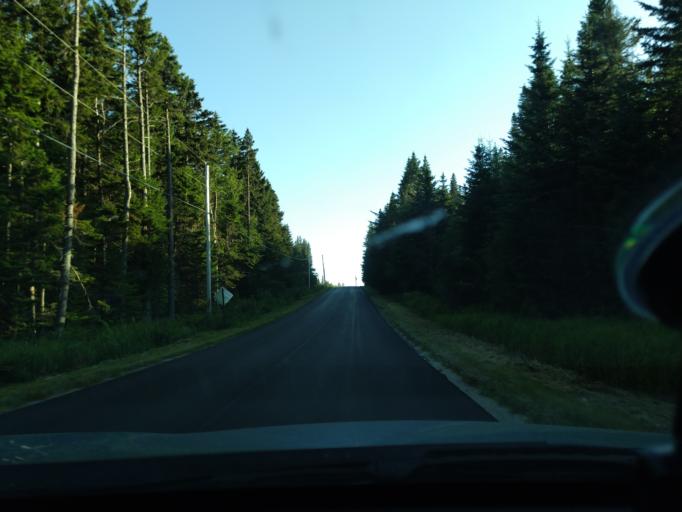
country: US
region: Maine
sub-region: Washington County
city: Machiasport
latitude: 44.6739
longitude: -67.1933
